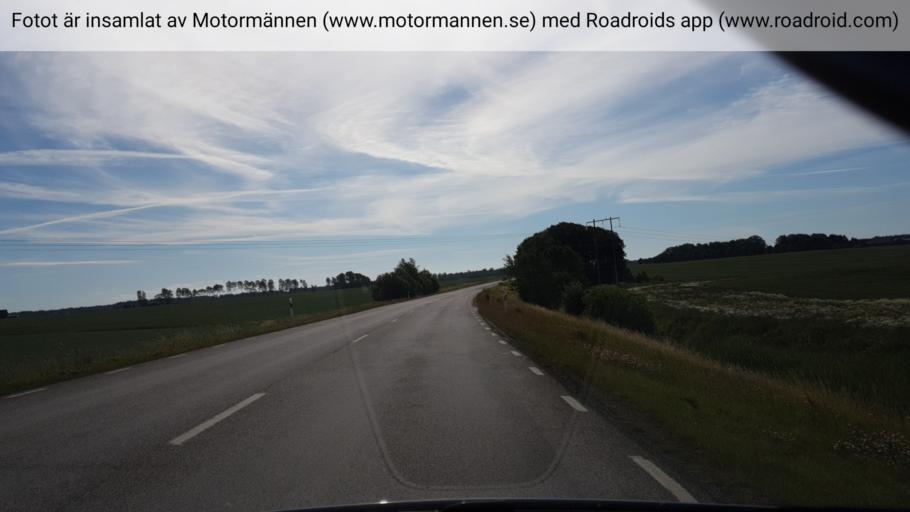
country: SE
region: Vaestra Goetaland
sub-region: Skovde Kommun
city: Skoevde
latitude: 58.3819
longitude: 13.9614
